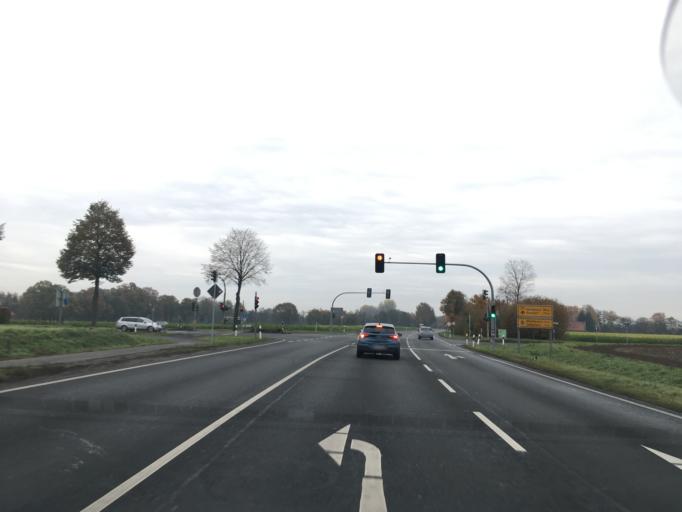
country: DE
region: North Rhine-Westphalia
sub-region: Regierungsbezirk Munster
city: Ostbevern
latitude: 52.0300
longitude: 7.8327
